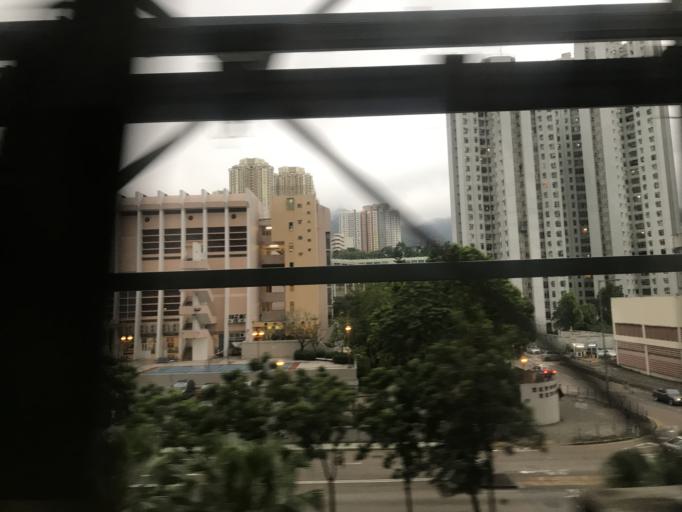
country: HK
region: Sha Tin
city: Sha Tin
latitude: 22.3717
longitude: 114.1765
